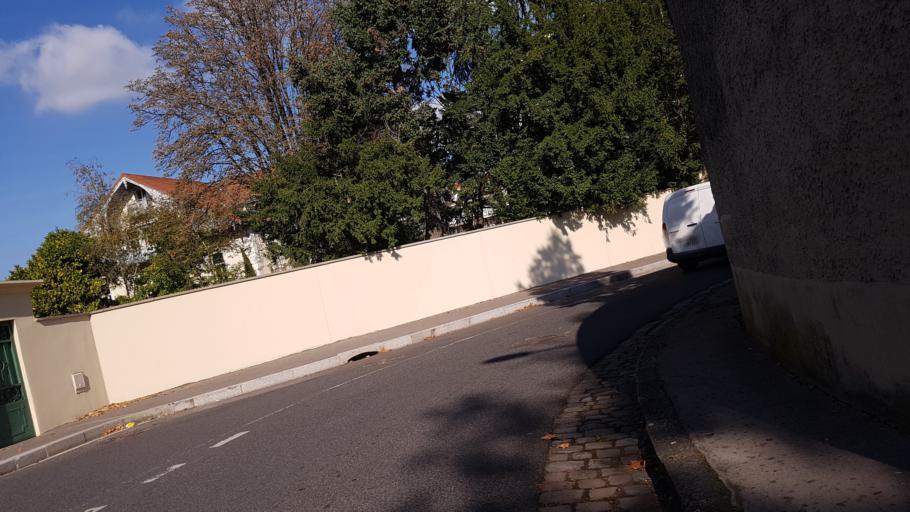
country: FR
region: Rhone-Alpes
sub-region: Departement du Rhone
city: Caluire-et-Cuire
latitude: 45.7834
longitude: 4.8180
